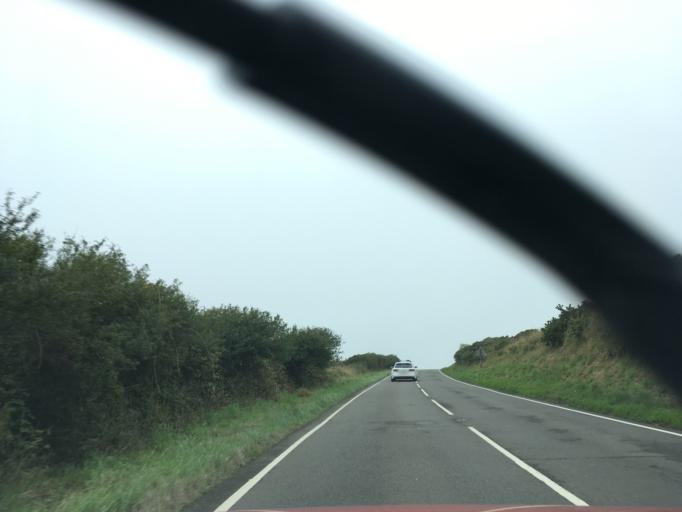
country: GB
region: Wales
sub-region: Pembrokeshire
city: Llanrhian
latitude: 51.8765
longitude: -5.1720
